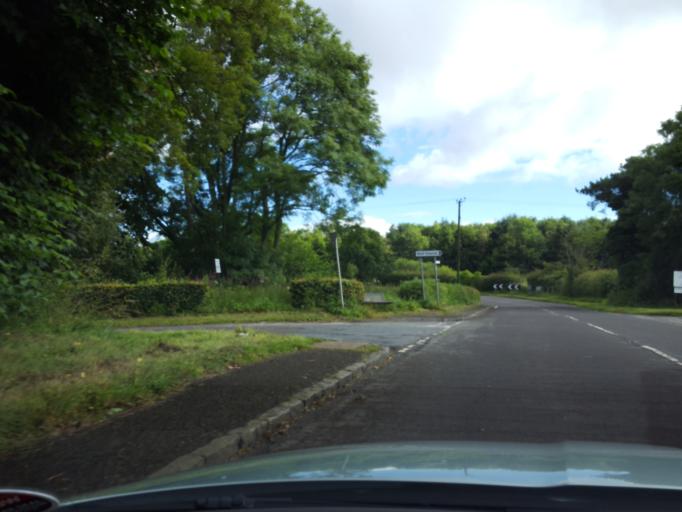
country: GB
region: Scotland
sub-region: West Lothian
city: Linlithgow
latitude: 55.9960
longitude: -3.6090
